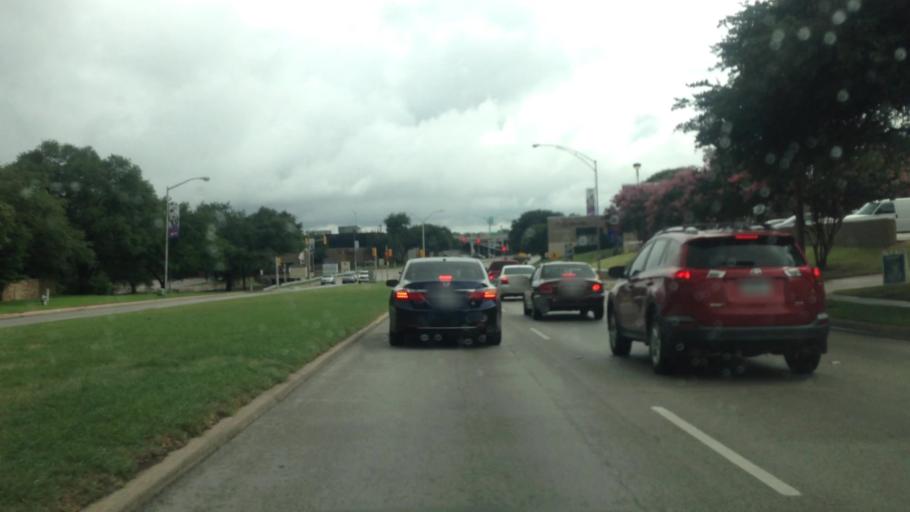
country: US
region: Texas
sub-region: Tarrant County
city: Edgecliff Village
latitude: 32.6841
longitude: -97.3925
